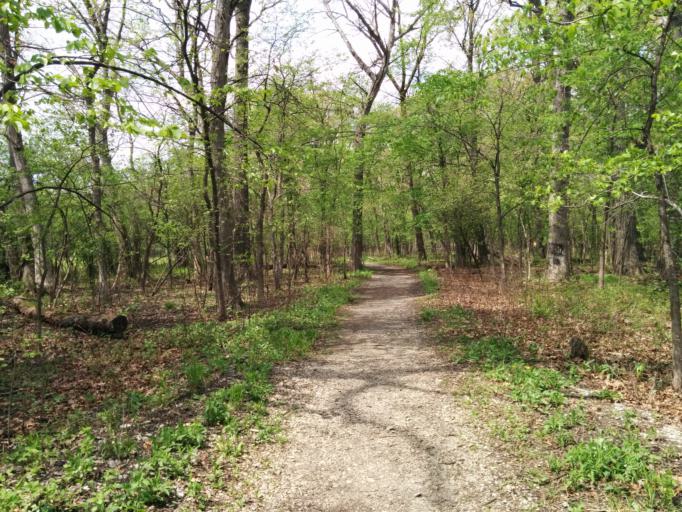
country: US
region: Illinois
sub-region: Cook County
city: River Forest
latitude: 41.8982
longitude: -87.8294
